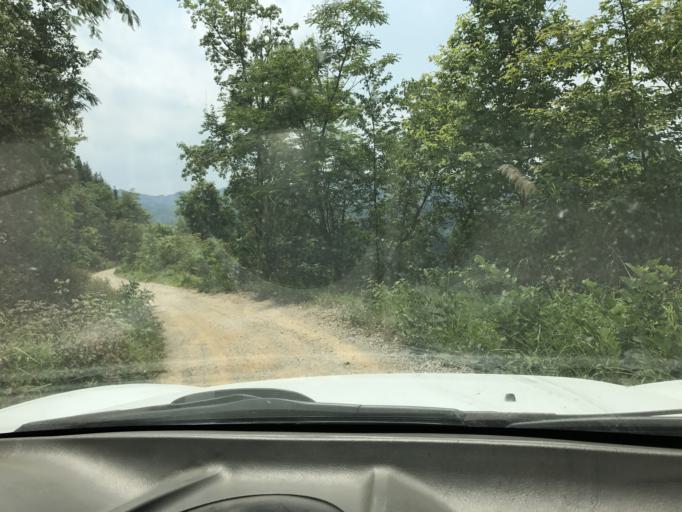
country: CN
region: Guangxi Zhuangzu Zizhiqu
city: Xinzhou
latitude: 24.9936
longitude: 105.9173
